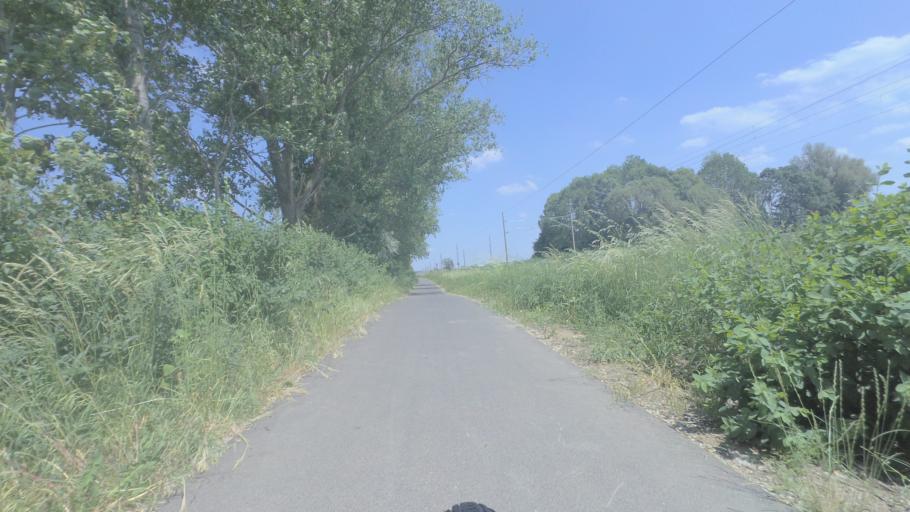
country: DE
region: Saxony-Anhalt
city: Wittenburg
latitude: 51.8295
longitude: 12.6133
